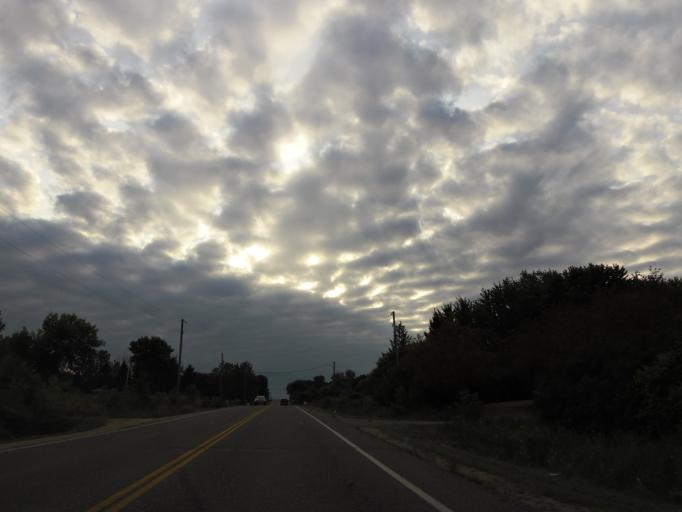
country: US
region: Minnesota
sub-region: Dakota County
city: Lakeville
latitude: 44.6561
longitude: -93.2216
